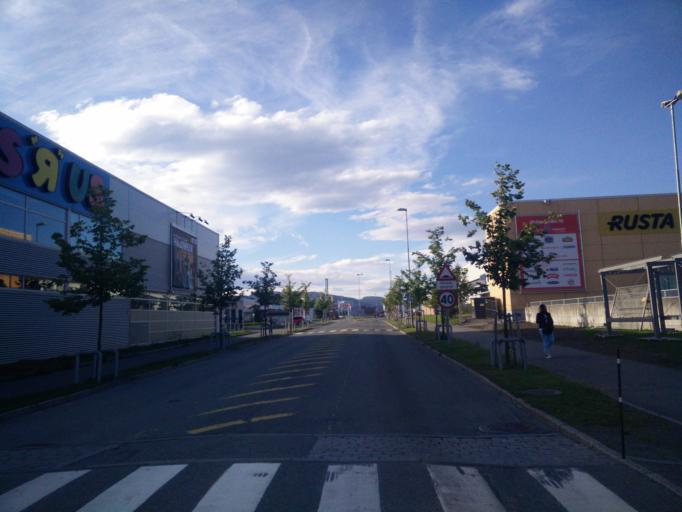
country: NO
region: Sor-Trondelag
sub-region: Trondheim
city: Trondheim
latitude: 63.3585
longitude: 10.3762
